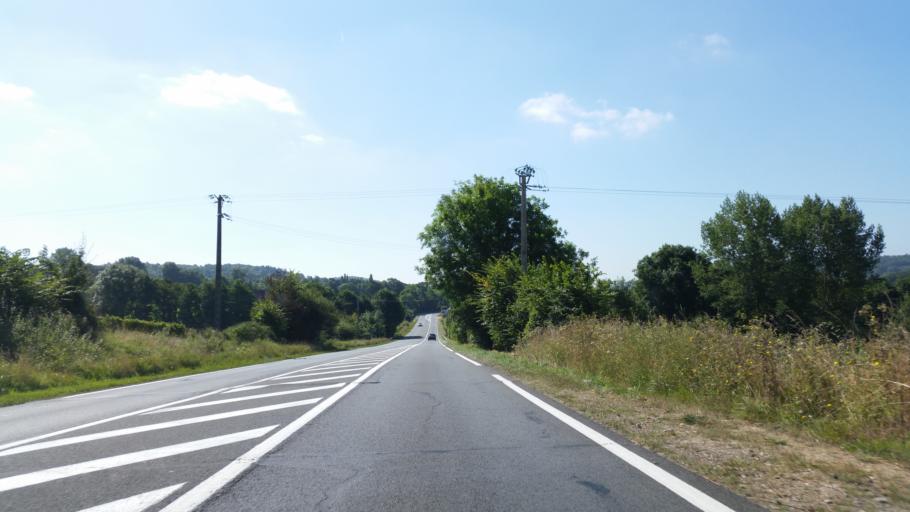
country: FR
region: Lower Normandy
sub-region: Departement du Calvados
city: Saint-Gatien-des-Bois
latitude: 49.2735
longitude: 0.2166
